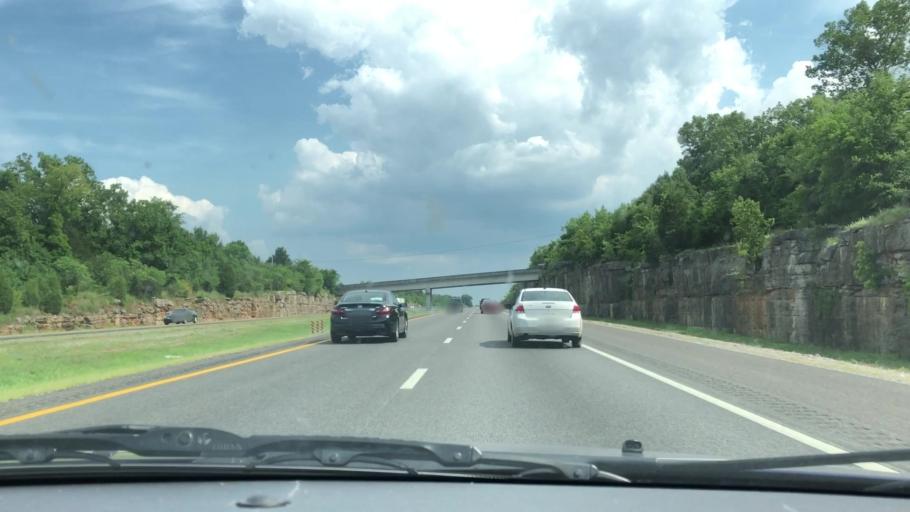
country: US
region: Tennessee
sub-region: Rutherford County
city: Smyrna
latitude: 35.9529
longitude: -86.4423
